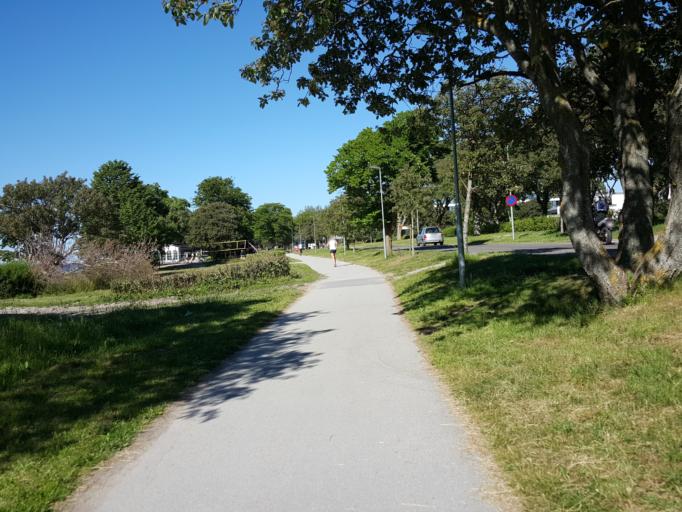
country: SE
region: Gotland
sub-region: Gotland
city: Visby
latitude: 57.6522
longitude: 18.3028
